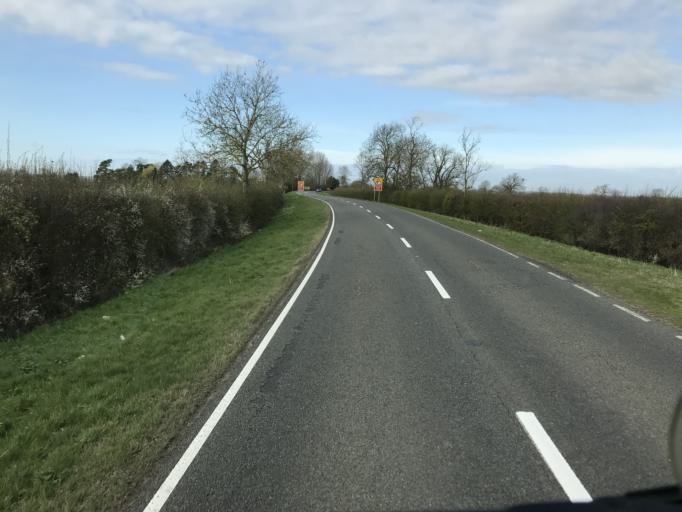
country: GB
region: England
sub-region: Lincolnshire
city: Market Rasen
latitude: 53.3955
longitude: -0.4132
